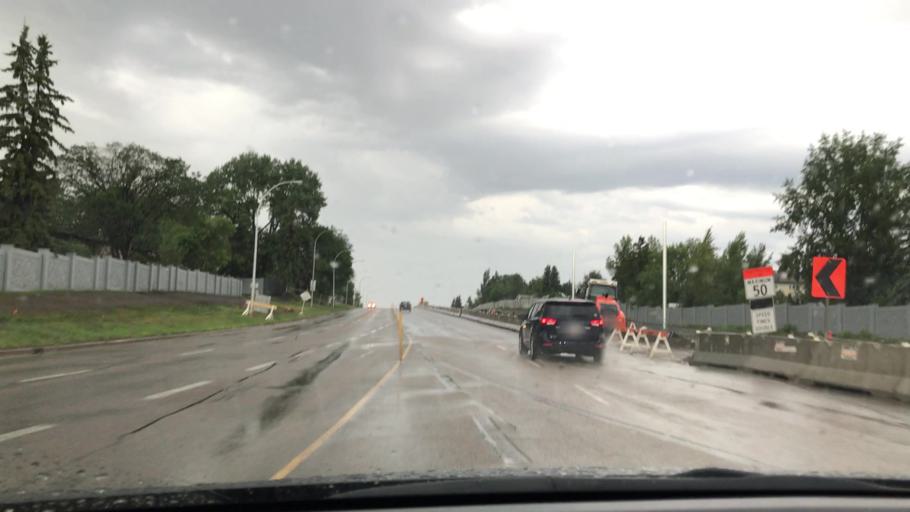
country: CA
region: Alberta
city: Edmonton
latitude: 53.4663
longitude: -113.4365
